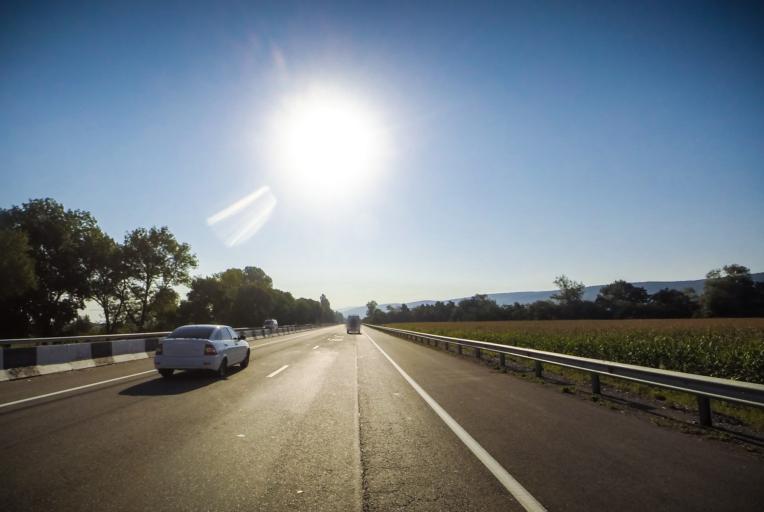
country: RU
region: North Ossetia
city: Zmeyskaya
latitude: 43.3229
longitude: 44.1207
